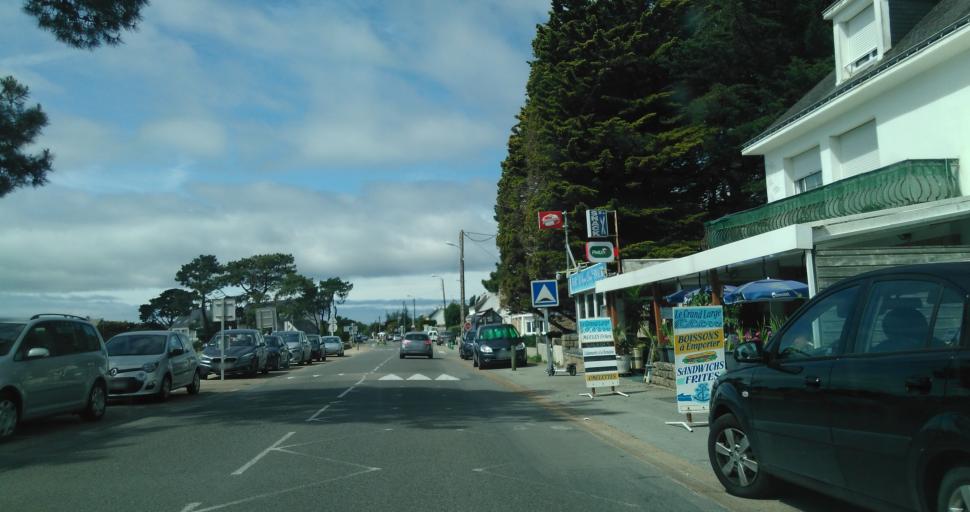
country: FR
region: Brittany
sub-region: Departement du Morbihan
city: La Trinite-sur-Mer
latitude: 47.5786
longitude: -3.0509
